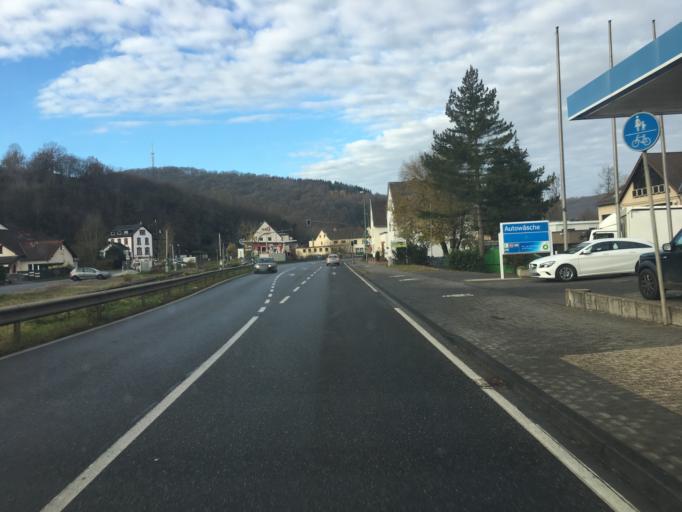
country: DE
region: North Rhine-Westphalia
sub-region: Regierungsbezirk Koln
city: Kall
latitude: 50.5706
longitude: 6.5063
